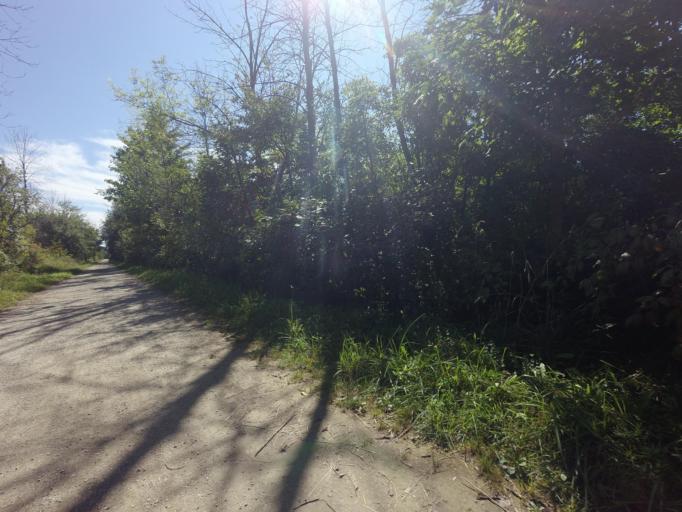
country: CA
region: Ontario
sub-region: Wellington County
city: Guelph
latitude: 43.6987
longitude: -80.3952
